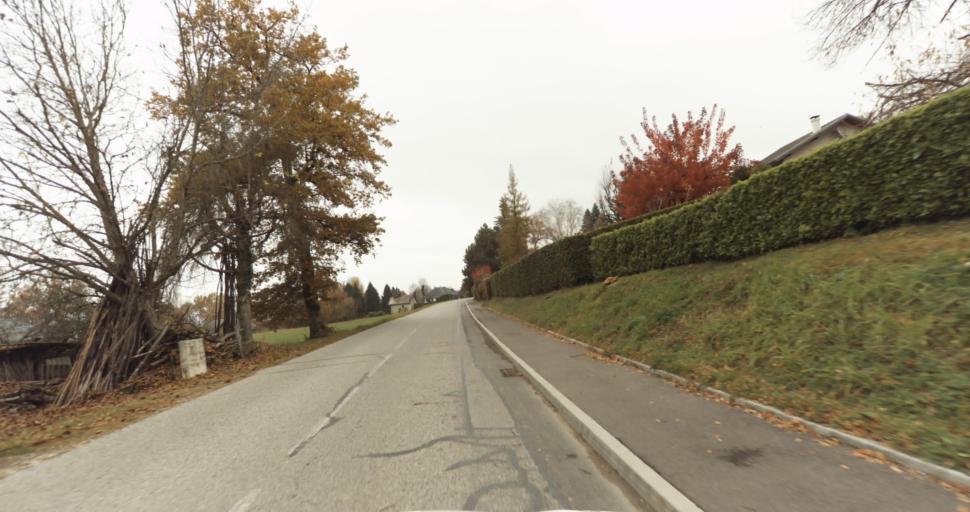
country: FR
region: Rhone-Alpes
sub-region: Departement de la Haute-Savoie
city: Saint-Felix
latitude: 45.7869
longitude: 5.9881
